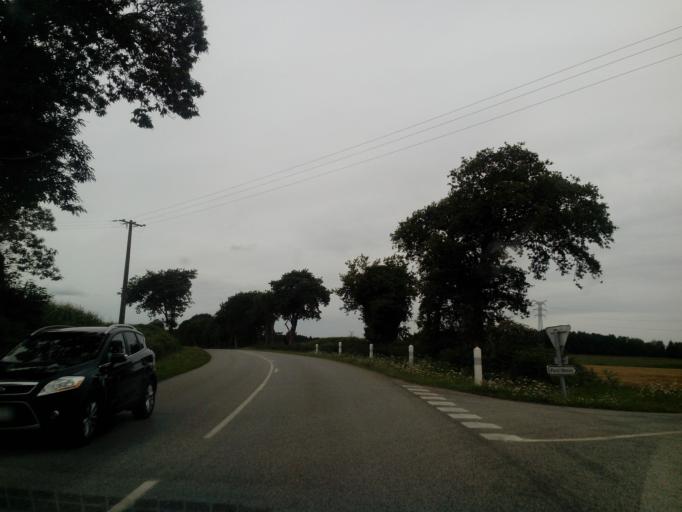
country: FR
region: Brittany
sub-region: Departement du Morbihan
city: Caudan
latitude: 47.8317
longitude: -3.3443
